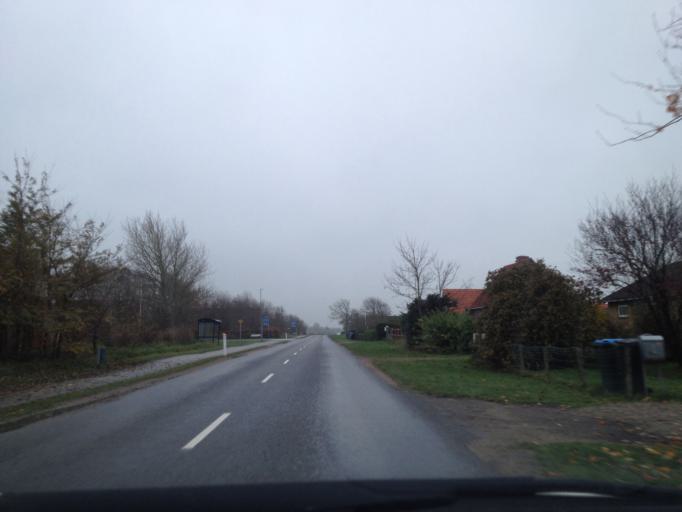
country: DK
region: South Denmark
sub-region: Tonder Kommune
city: Sherrebek
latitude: 55.1204
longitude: 8.7571
